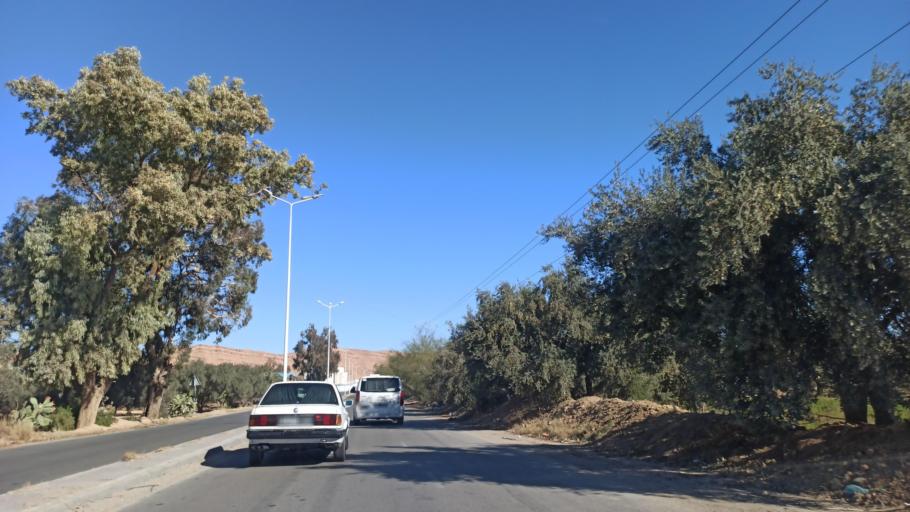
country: TN
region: Gafsa
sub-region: Gafsa Municipality
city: Gafsa
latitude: 34.4189
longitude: 8.7443
